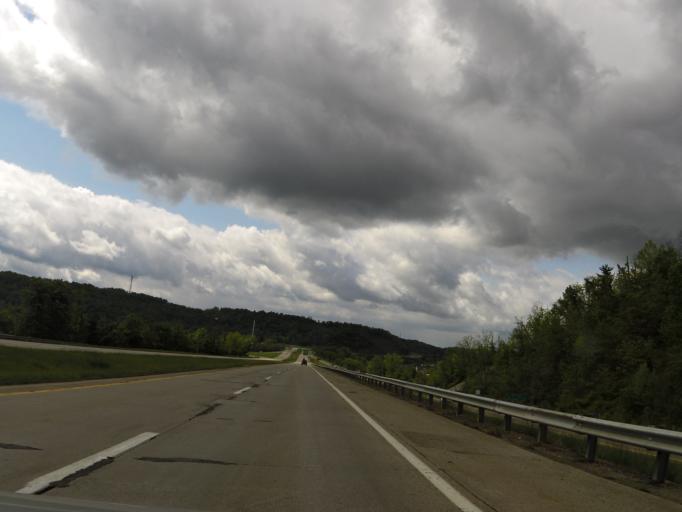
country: US
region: Ohio
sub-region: Athens County
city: Athens
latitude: 39.3407
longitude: -82.0813
